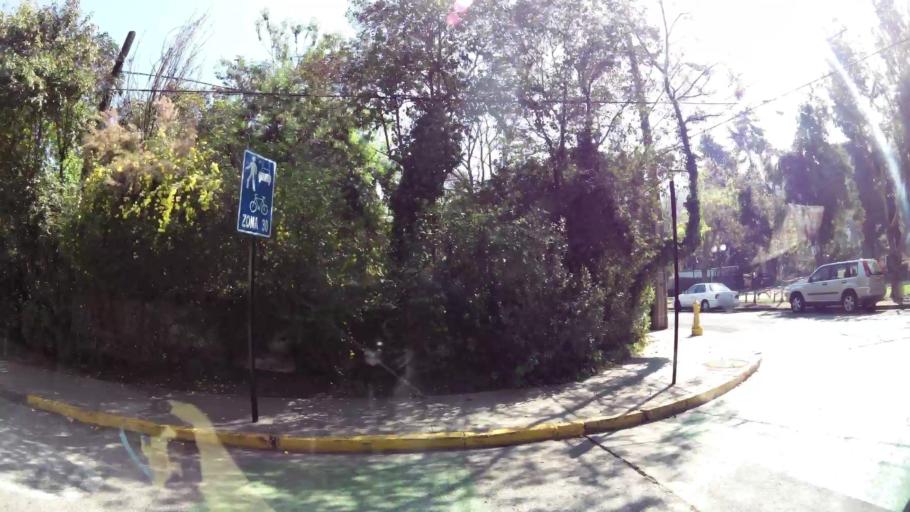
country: CL
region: Santiago Metropolitan
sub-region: Provincia de Santiago
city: Santiago
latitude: -33.4155
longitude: -70.6147
